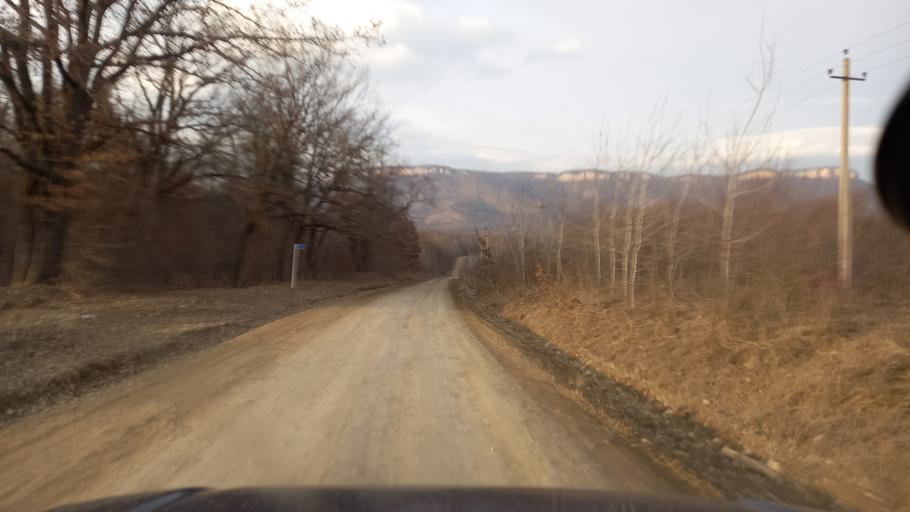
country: RU
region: Adygeya
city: Kamennomostskiy
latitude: 44.1993
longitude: 40.2499
